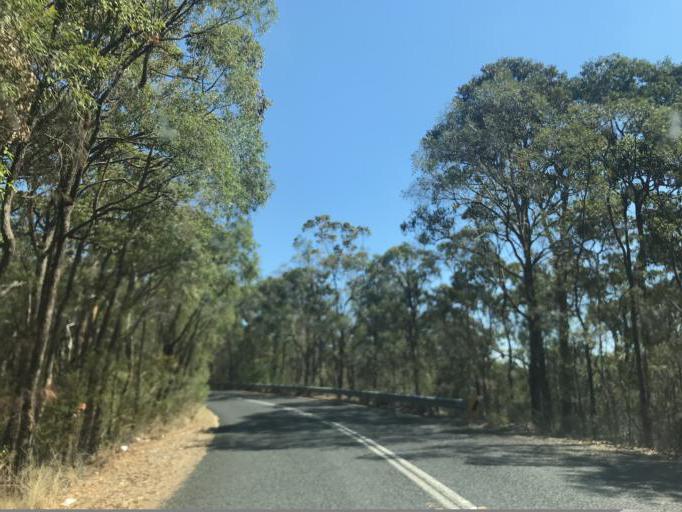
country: AU
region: New South Wales
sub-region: Hawkesbury
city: Pitt Town
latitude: -33.4498
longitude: 150.8708
